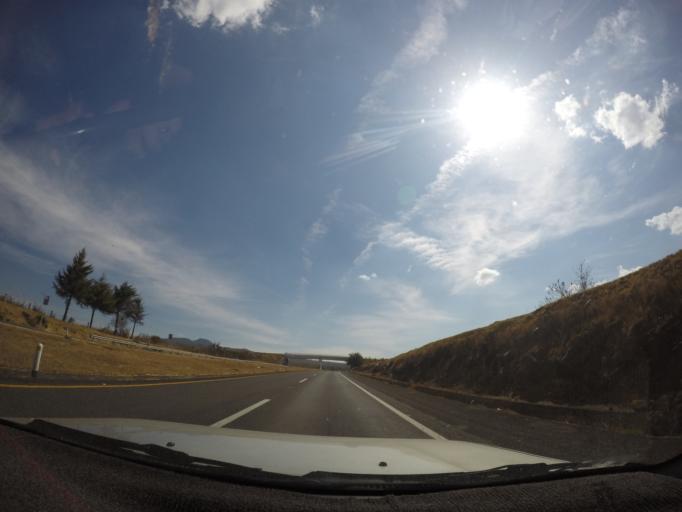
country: MX
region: Michoacan
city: Panindicuaro de la Reforma
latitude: 19.9980
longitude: -101.8710
